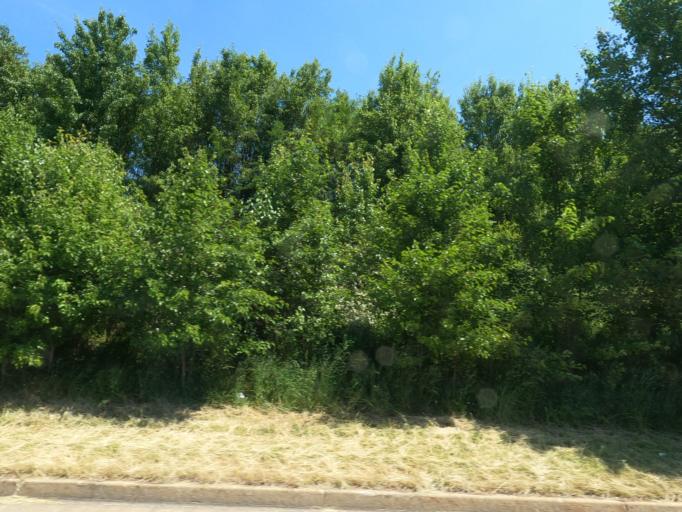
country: US
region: Maryland
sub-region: Howard County
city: Savage
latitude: 39.1769
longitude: -76.8202
